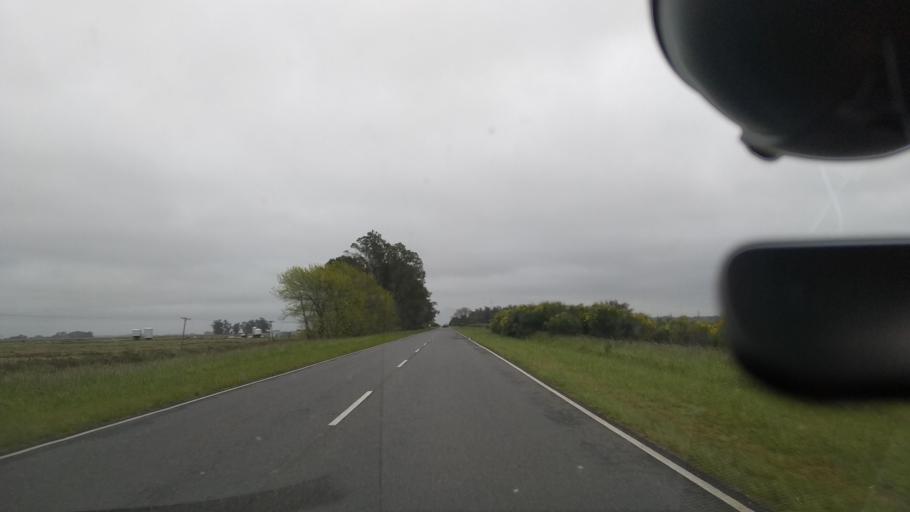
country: AR
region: Buenos Aires
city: Veronica
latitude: -35.4592
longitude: -57.3298
